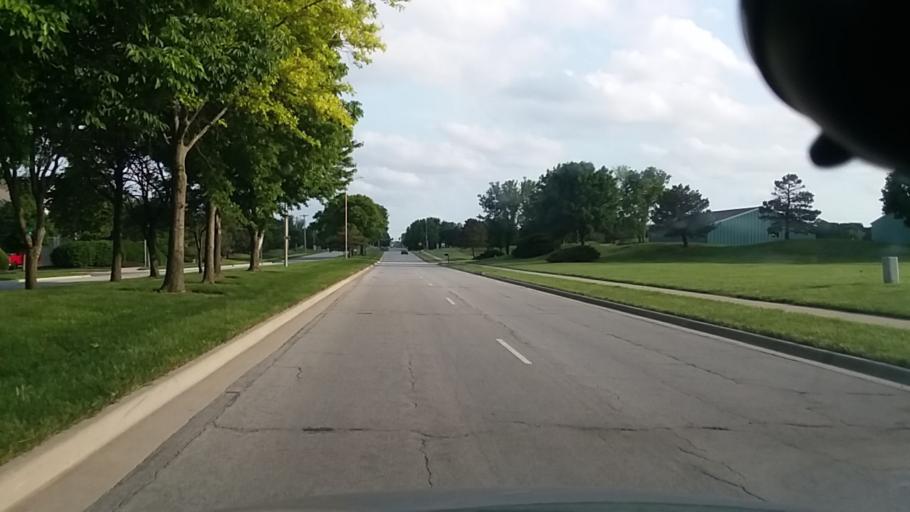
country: US
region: Kansas
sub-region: Johnson County
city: Olathe
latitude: 38.9536
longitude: -94.8162
